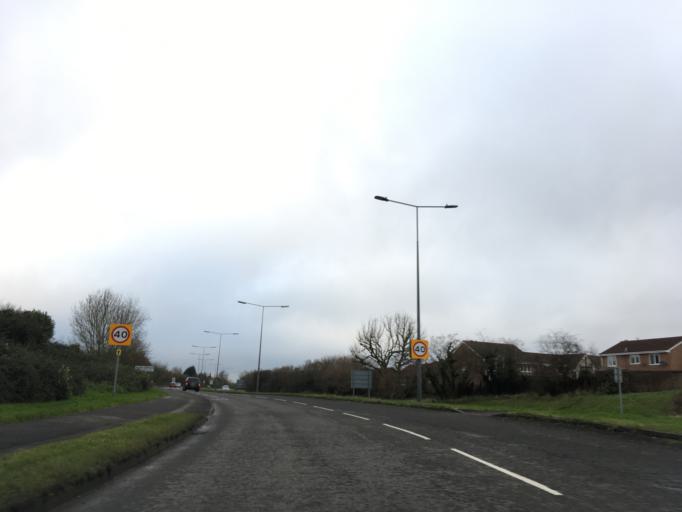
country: GB
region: England
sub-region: South Gloucestershire
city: Stoke Gifford
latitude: 51.5213
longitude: -2.5315
